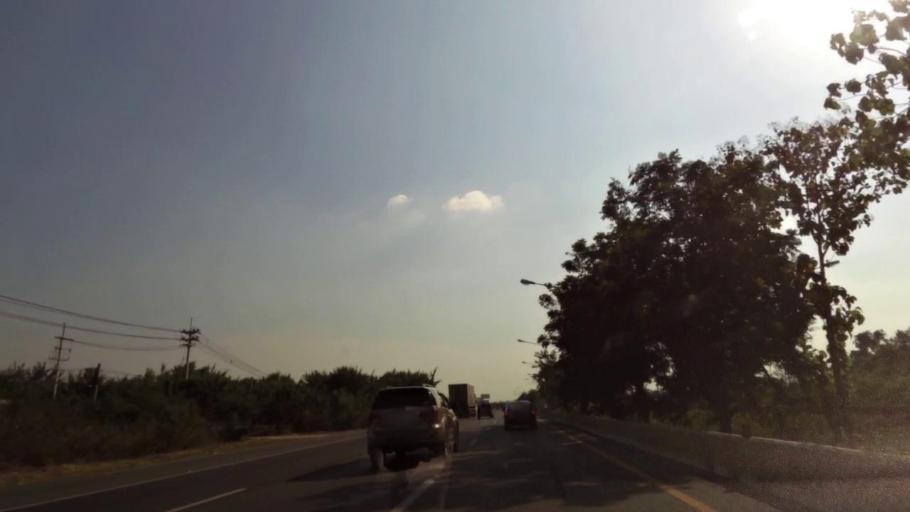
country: TH
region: Ang Thong
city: Ban Thai Tan
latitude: 14.6215
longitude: 100.4712
